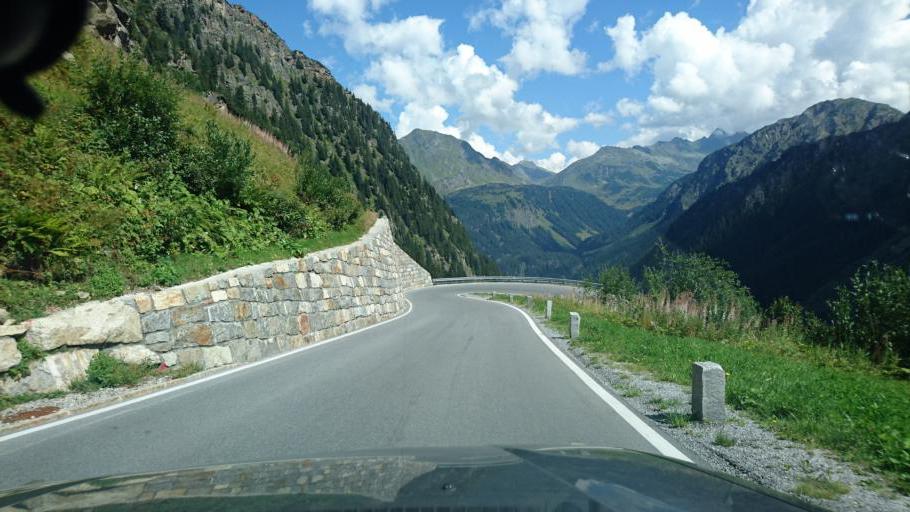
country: AT
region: Vorarlberg
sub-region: Politischer Bezirk Bludenz
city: Gaschurn
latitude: 46.9432
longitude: 10.0589
